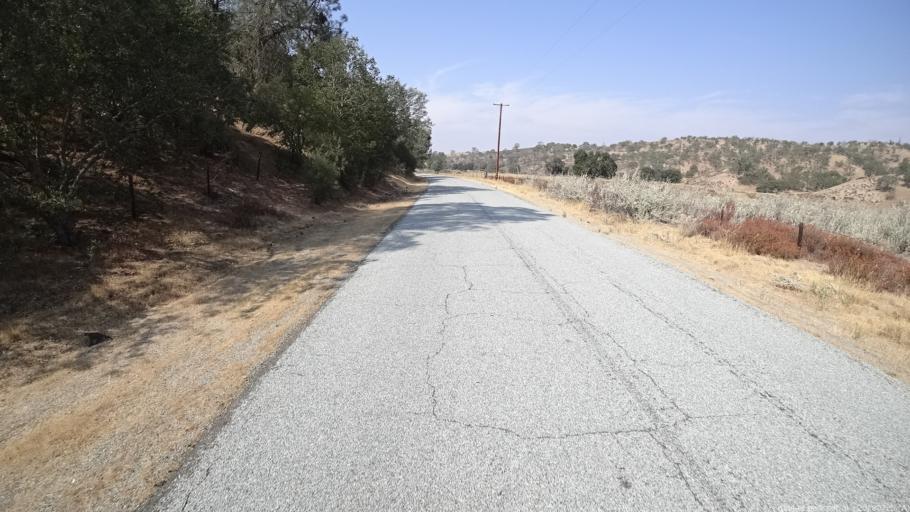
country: US
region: California
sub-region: San Luis Obispo County
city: San Miguel
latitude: 35.8559
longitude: -120.6026
